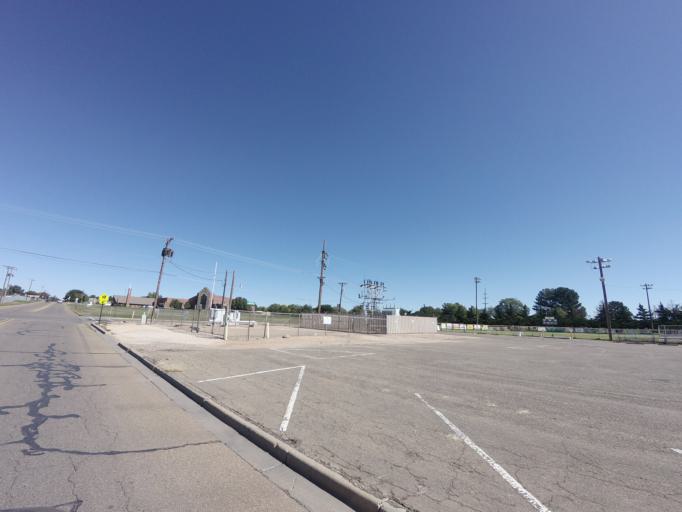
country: US
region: New Mexico
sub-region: Curry County
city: Clovis
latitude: 34.4116
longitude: -103.1877
